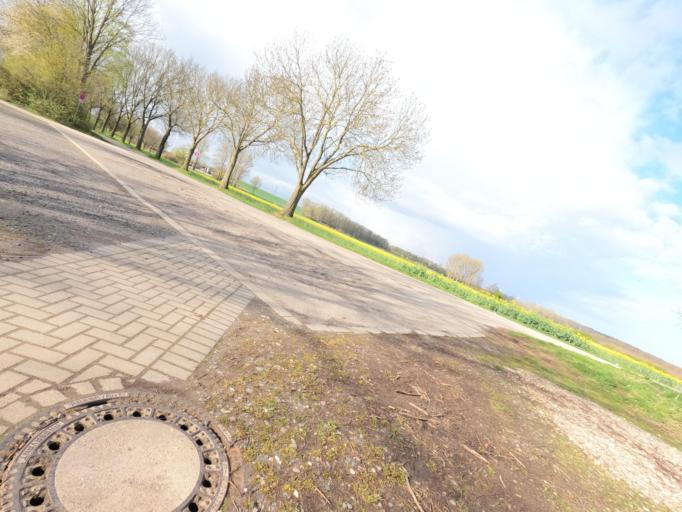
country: DE
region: North Rhine-Westphalia
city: Huckelhoven
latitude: 51.0183
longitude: 6.2249
